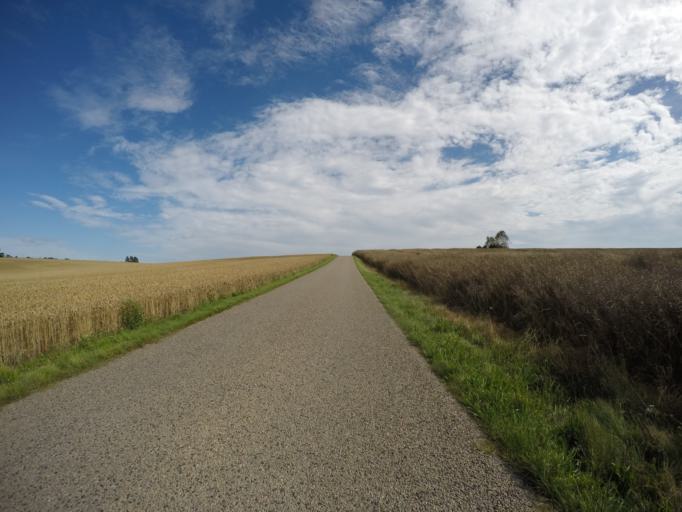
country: SE
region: Skane
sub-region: Simrishamns Kommun
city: Simrishamn
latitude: 55.4942
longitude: 14.2455
